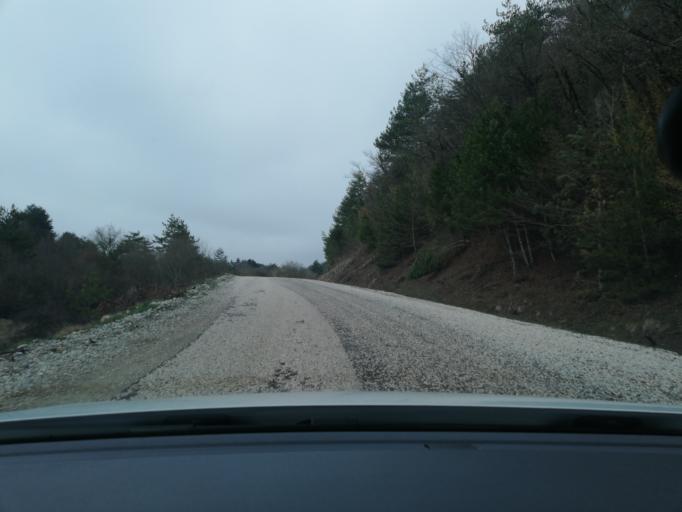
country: TR
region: Bolu
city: Bolu
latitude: 40.6605
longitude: 31.4735
